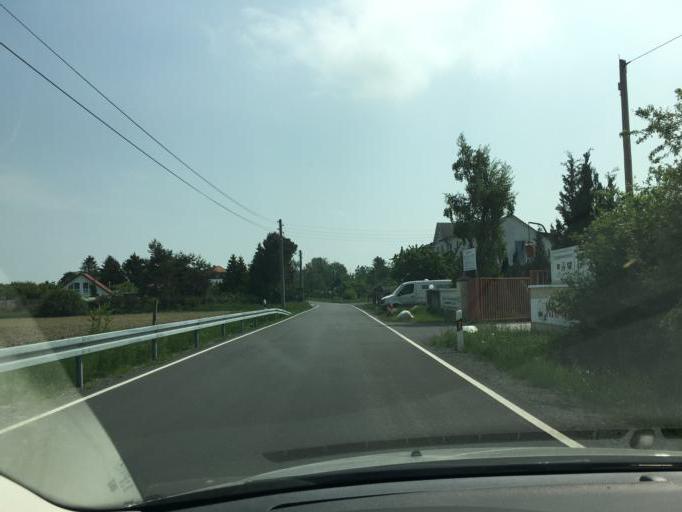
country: DE
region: Saxony
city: Grossposna
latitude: 51.2936
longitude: 12.5005
